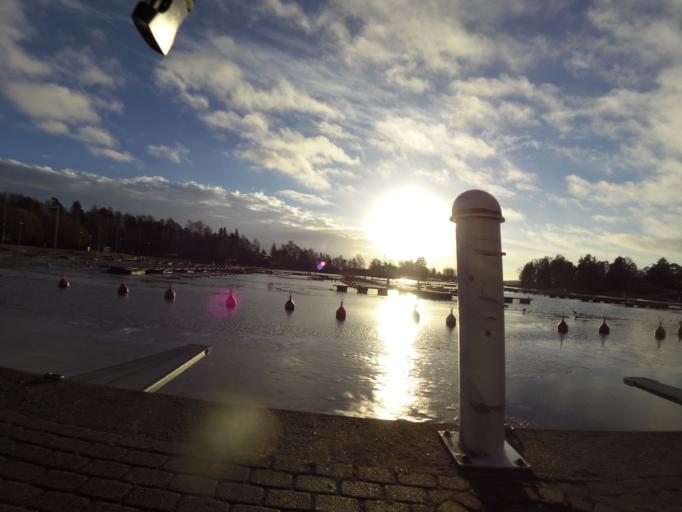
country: FI
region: Uusimaa
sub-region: Helsinki
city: Koukkuniemi
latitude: 60.1577
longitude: 24.7699
